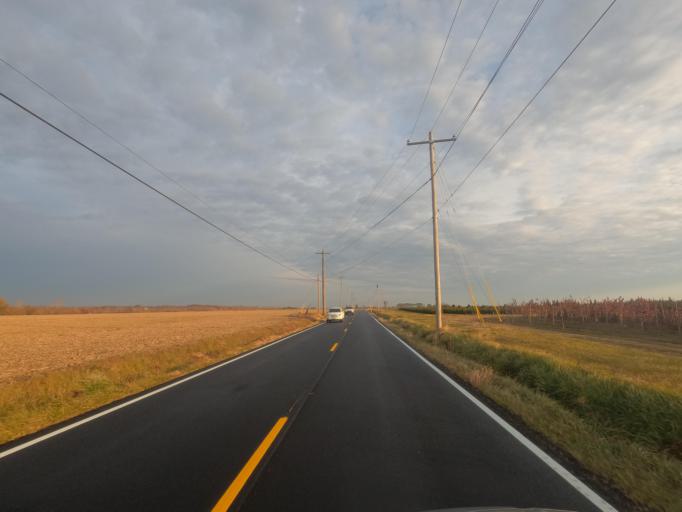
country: US
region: Delaware
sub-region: New Castle County
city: Townsend
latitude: 39.2821
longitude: -75.8370
